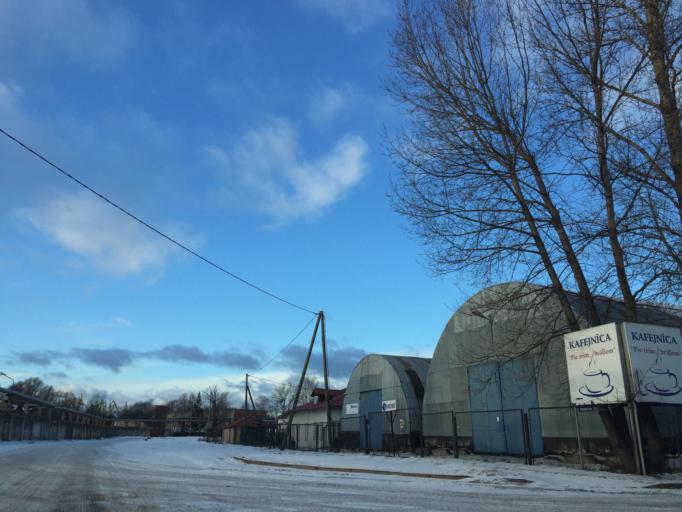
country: LV
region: Riga
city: Riga
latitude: 56.9817
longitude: 24.1107
